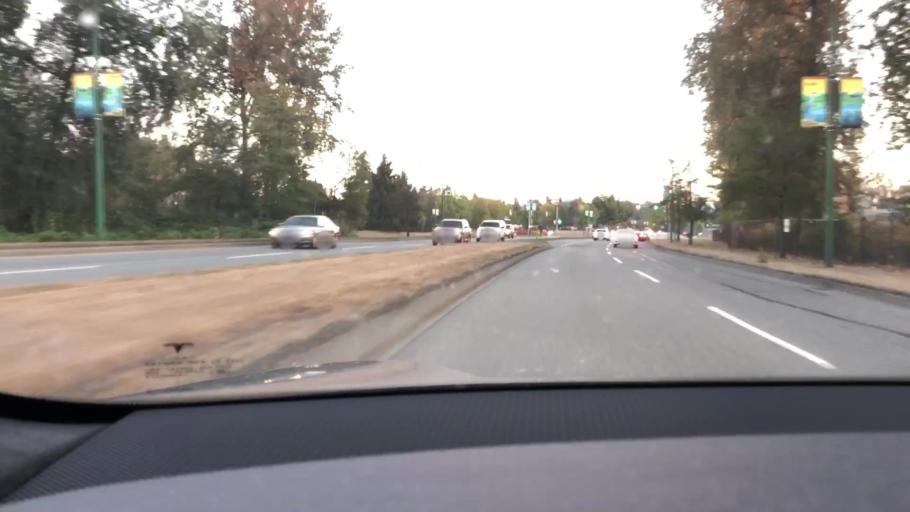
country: CA
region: British Columbia
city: Burnaby
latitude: 49.2576
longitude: -122.9640
